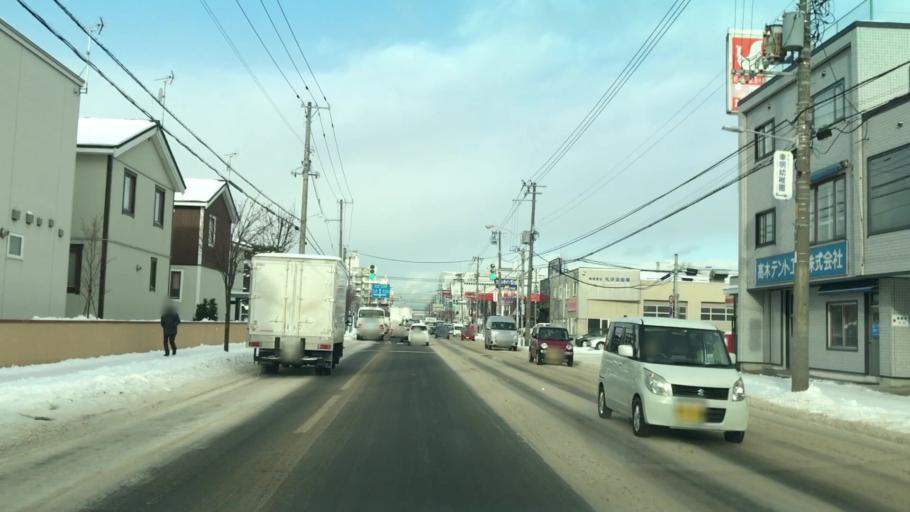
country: JP
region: Hokkaido
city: Sapporo
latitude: 43.0929
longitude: 141.3051
